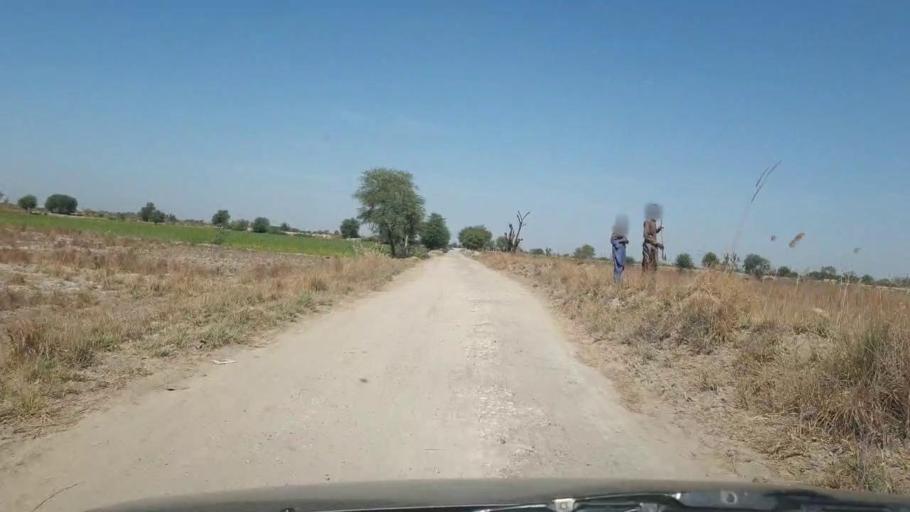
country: PK
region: Sindh
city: Dhoro Naro
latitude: 25.4546
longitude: 69.6085
